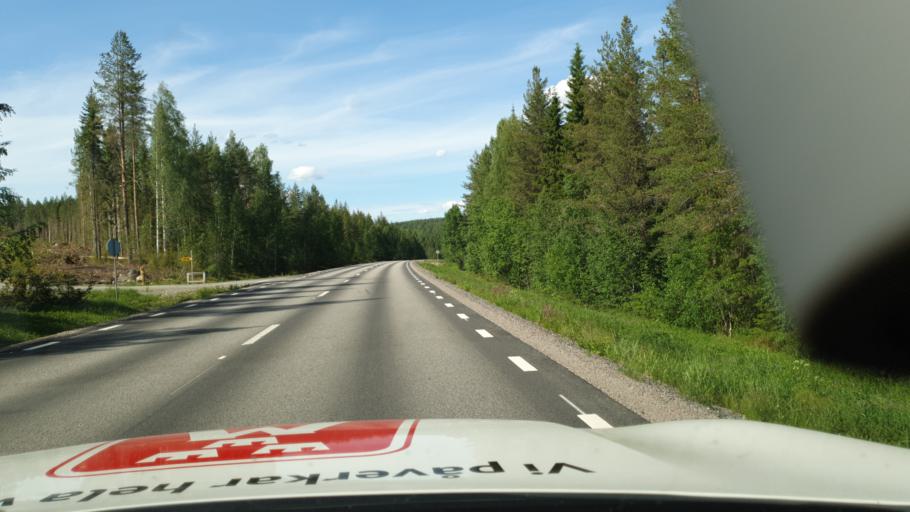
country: SE
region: Vaesterbotten
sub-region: Skelleftea Kommun
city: Boliden
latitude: 64.8896
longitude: 20.3779
